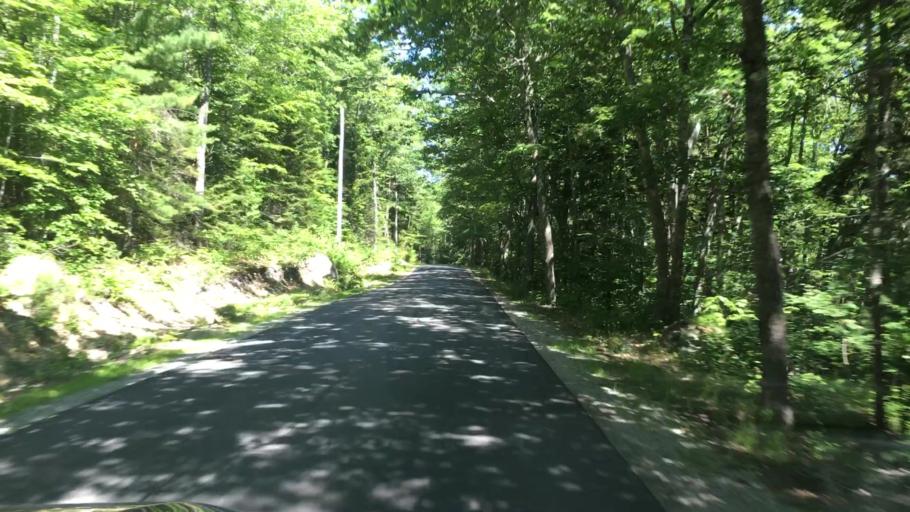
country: US
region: Maine
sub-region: Hancock County
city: Sedgwick
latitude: 44.3354
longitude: -68.6614
